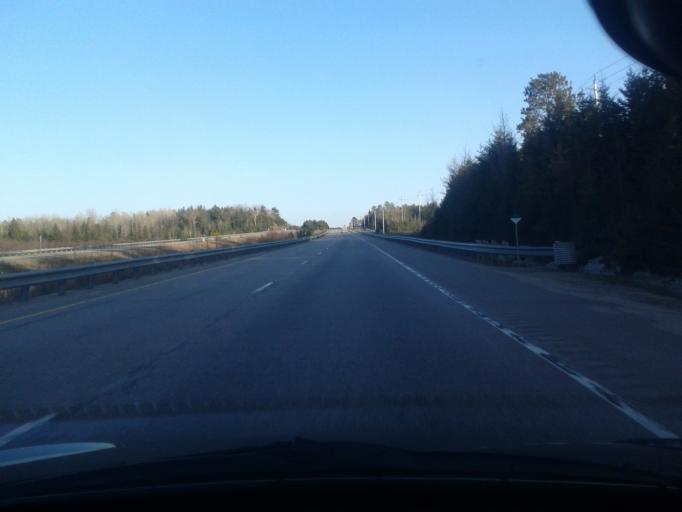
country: CA
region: Ontario
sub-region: Nipissing District
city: North Bay
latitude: 46.2527
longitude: -79.3750
